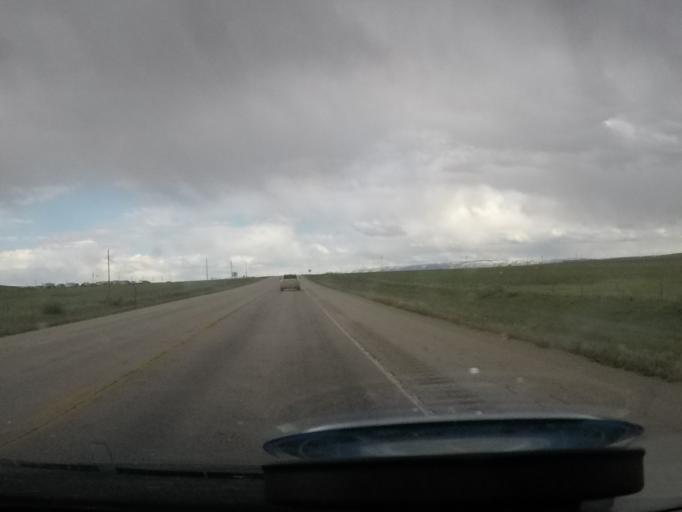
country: US
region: Wyoming
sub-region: Natrona County
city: Mills
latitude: 42.9576
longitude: -106.6525
